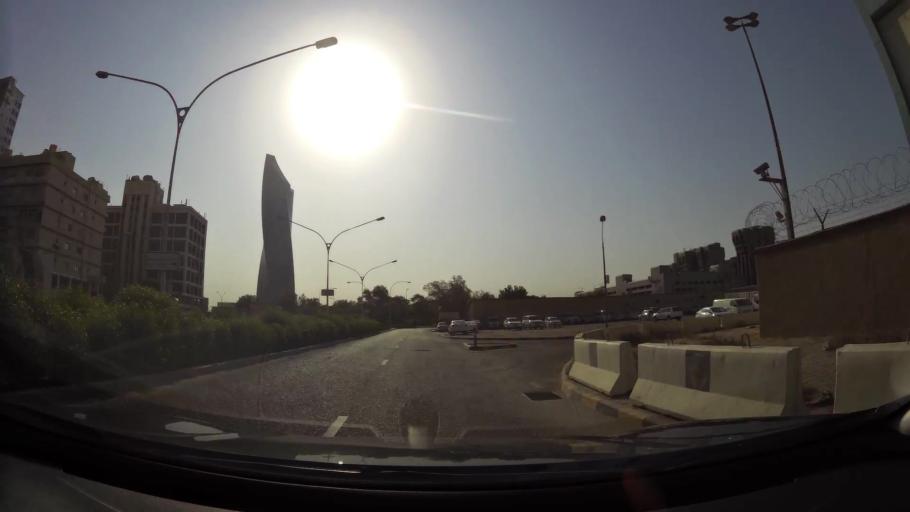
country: KW
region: Al Asimah
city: Kuwait City
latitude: 29.3723
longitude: 47.9869
